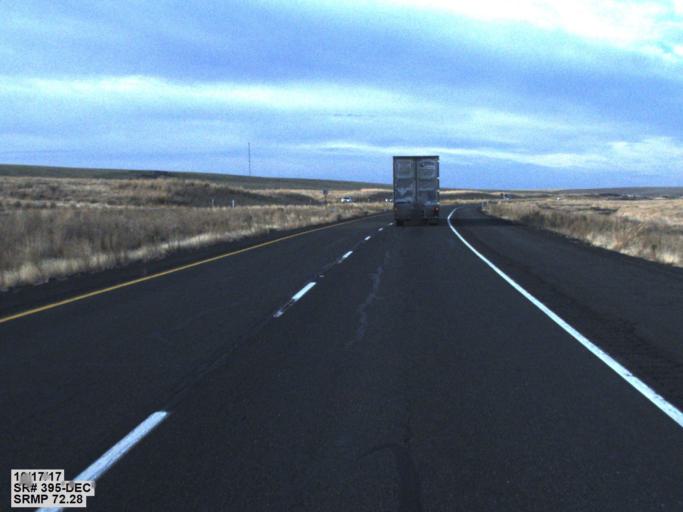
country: US
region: Washington
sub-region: Franklin County
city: Connell
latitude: 46.8394
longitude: -118.6481
